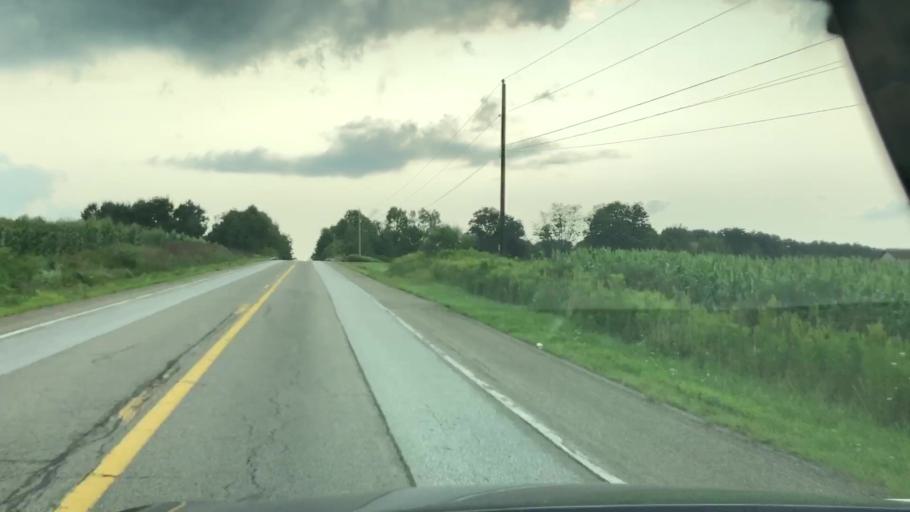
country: US
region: Pennsylvania
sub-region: Erie County
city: Union City
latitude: 41.9924
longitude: -79.8154
